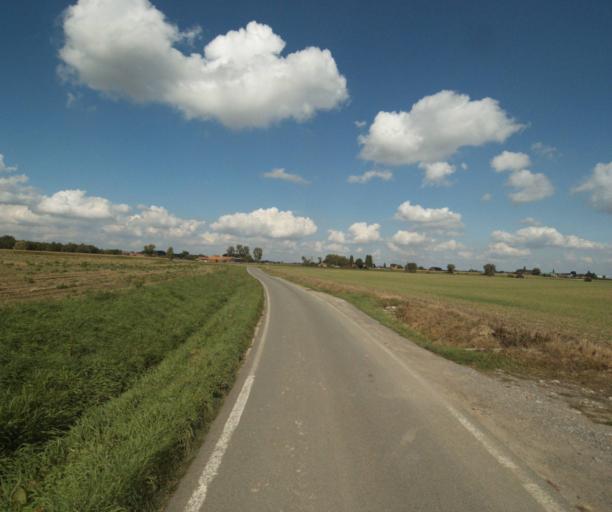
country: FR
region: Nord-Pas-de-Calais
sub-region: Departement du Nord
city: La Bassee
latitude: 50.5476
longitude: 2.8078
